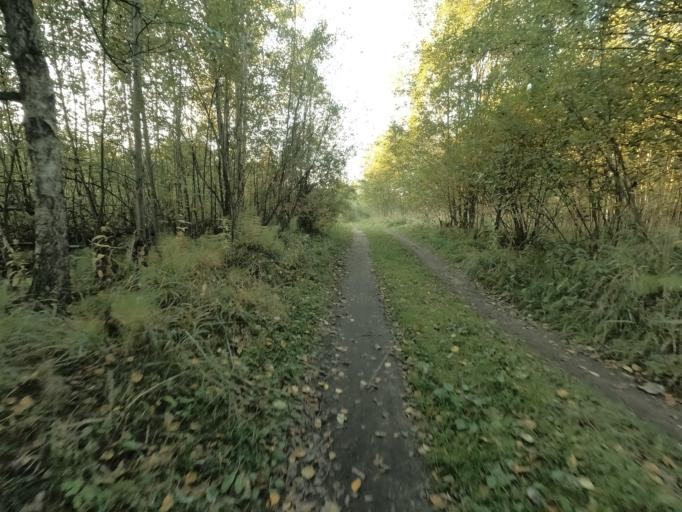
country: RU
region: Leningrad
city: Nikol'skoye
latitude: 59.7139
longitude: 30.7976
